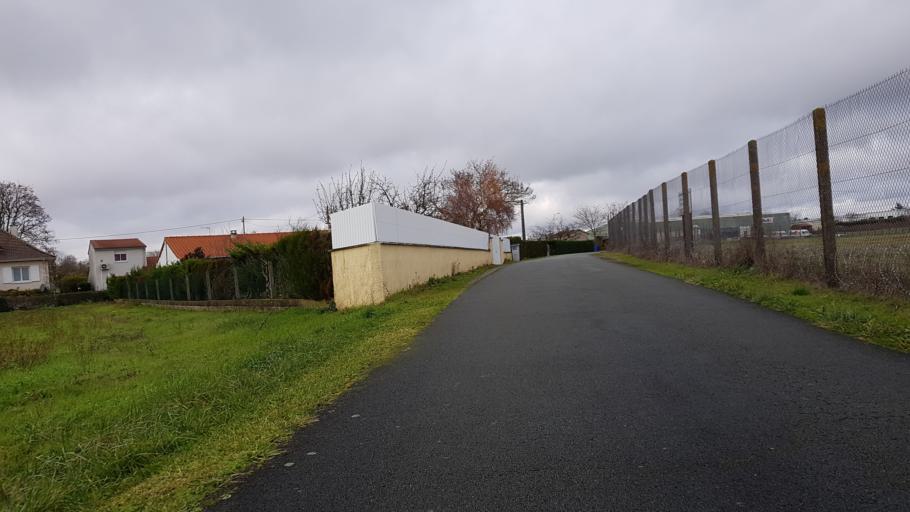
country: FR
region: Poitou-Charentes
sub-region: Departement de la Vienne
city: Chasseneuil-du-Poitou
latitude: 46.6542
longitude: 0.3732
